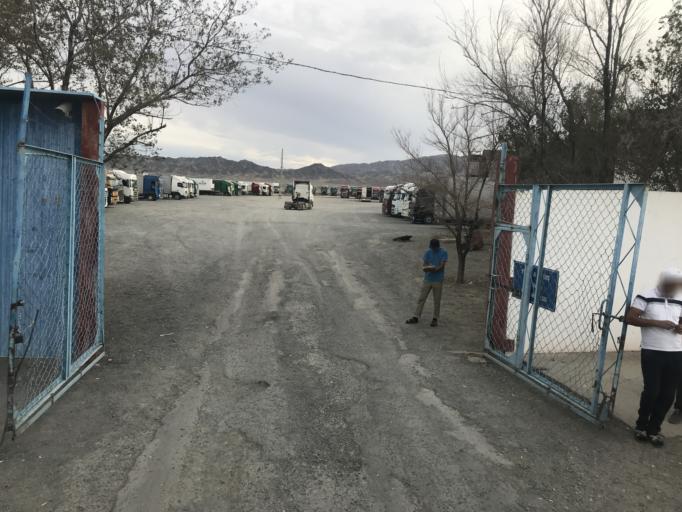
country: KZ
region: Almaty Oblysy
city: Dostyq
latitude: 45.2584
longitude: 82.4683
